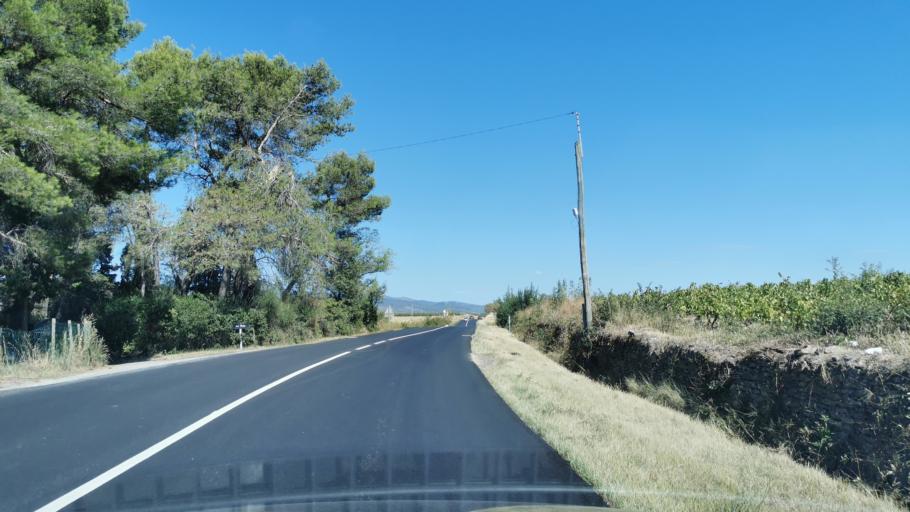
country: FR
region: Languedoc-Roussillon
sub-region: Departement de l'Aude
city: Conques-sur-Orbiel
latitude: 43.2756
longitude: 2.4260
